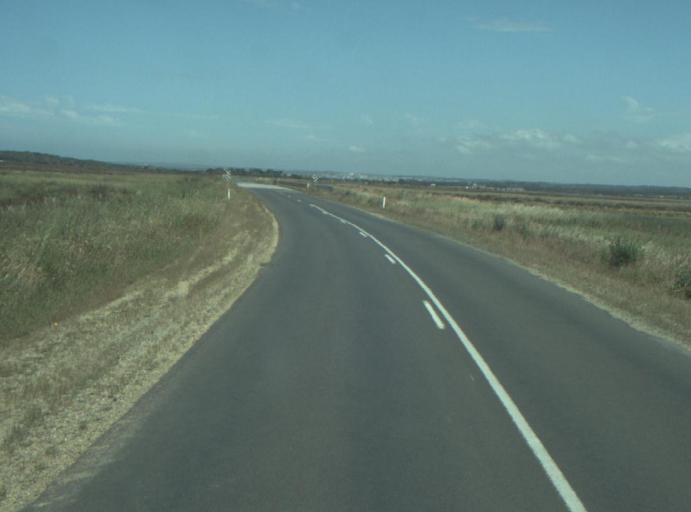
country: AU
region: Victoria
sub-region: Greater Geelong
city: Breakwater
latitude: -38.2862
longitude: 144.3985
